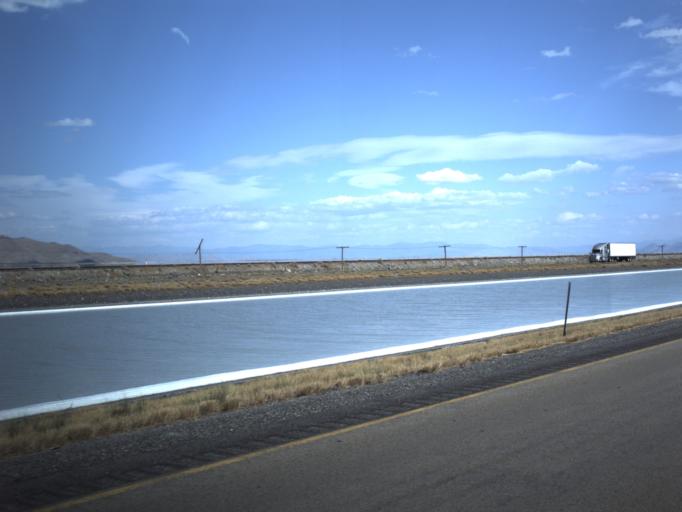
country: US
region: Utah
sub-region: Tooele County
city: Grantsville
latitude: 40.7335
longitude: -112.6014
